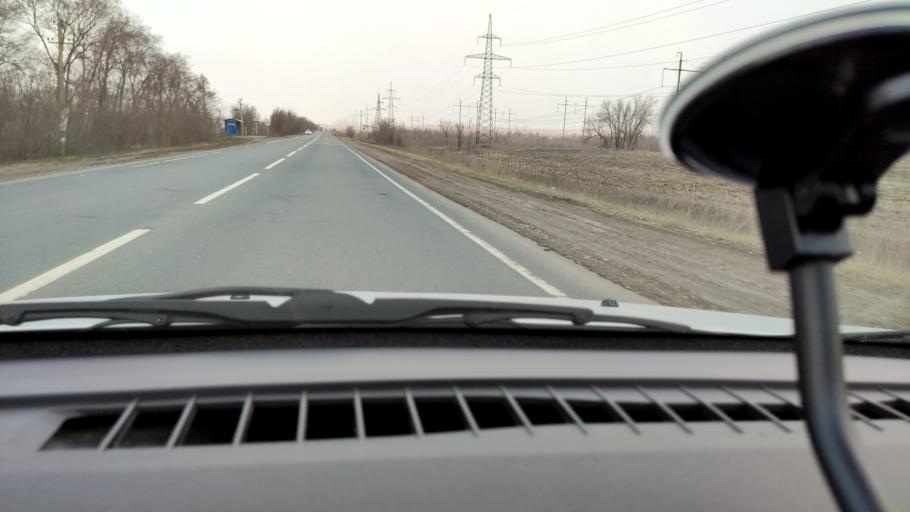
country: RU
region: Samara
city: Dubovyy Umet
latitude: 53.0814
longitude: 50.3902
